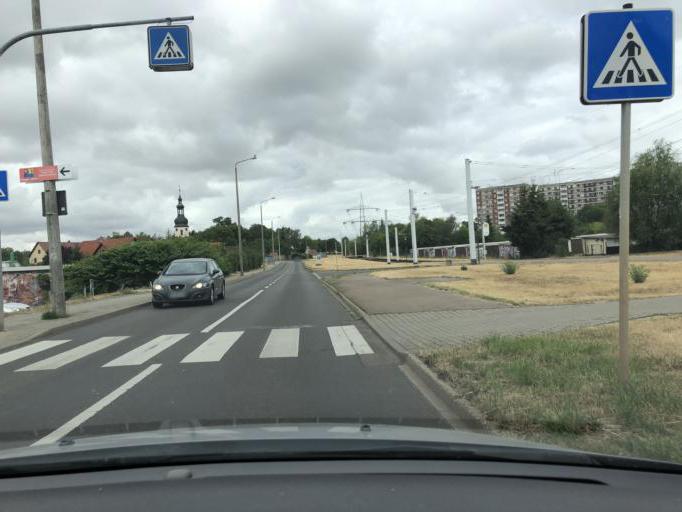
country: DE
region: Saxony-Anhalt
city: Schkopau
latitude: 51.4322
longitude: 11.9671
